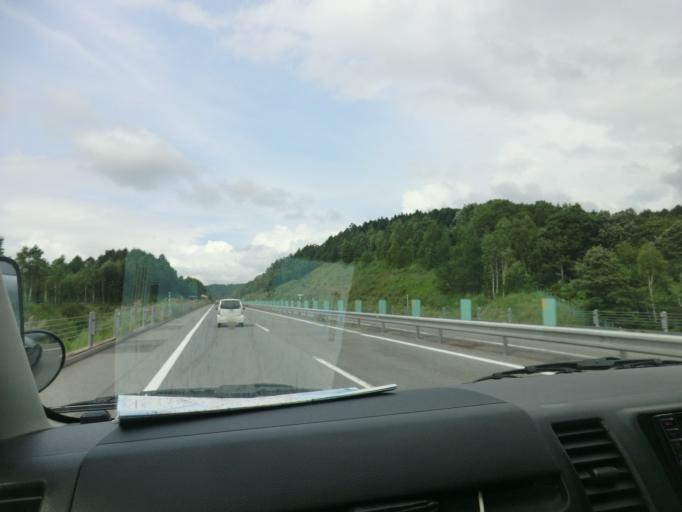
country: JP
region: Hokkaido
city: Fukagawa
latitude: 43.7505
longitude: 142.1665
